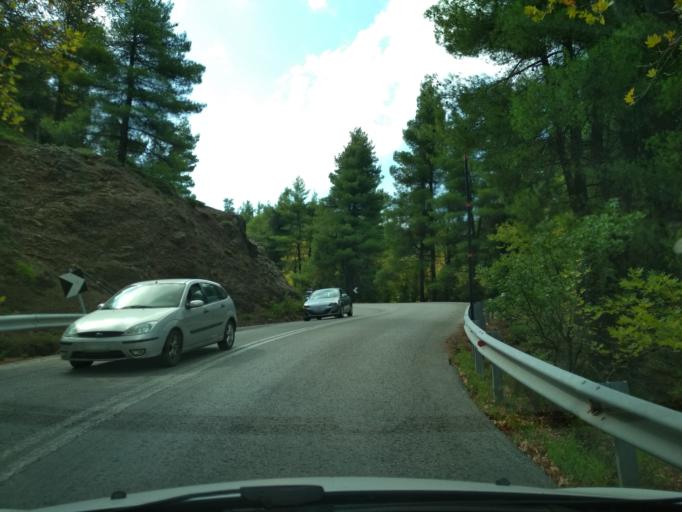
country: GR
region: Central Greece
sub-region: Nomos Evvoias
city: Politika
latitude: 38.6686
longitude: 23.5580
